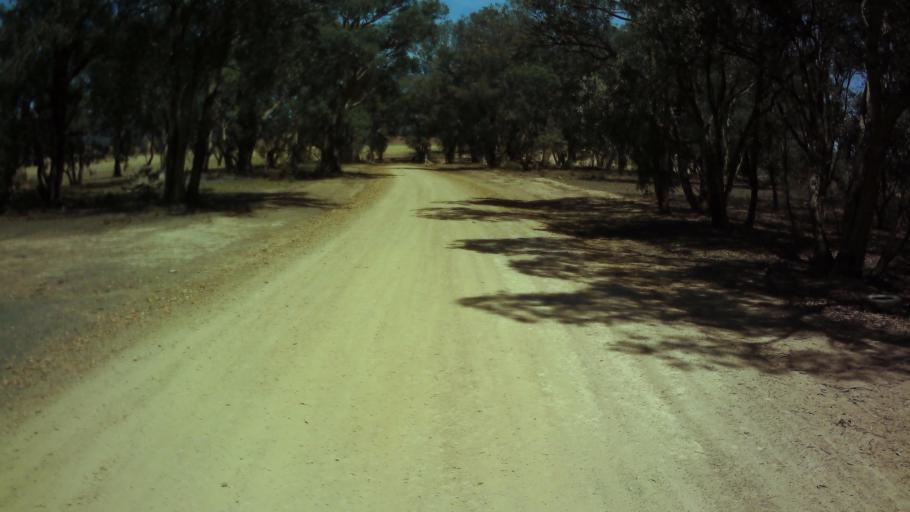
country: AU
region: New South Wales
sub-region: Weddin
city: Grenfell
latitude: -33.9687
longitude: 148.1406
